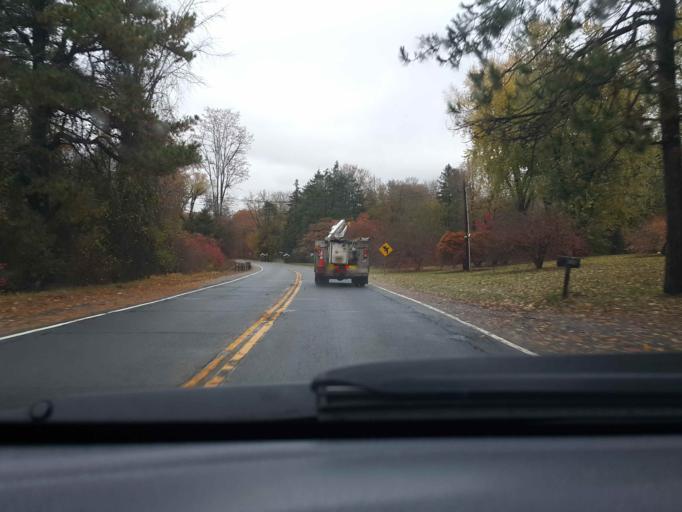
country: US
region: Connecticut
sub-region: Middlesex County
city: Durham
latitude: 41.4513
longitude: -72.6811
